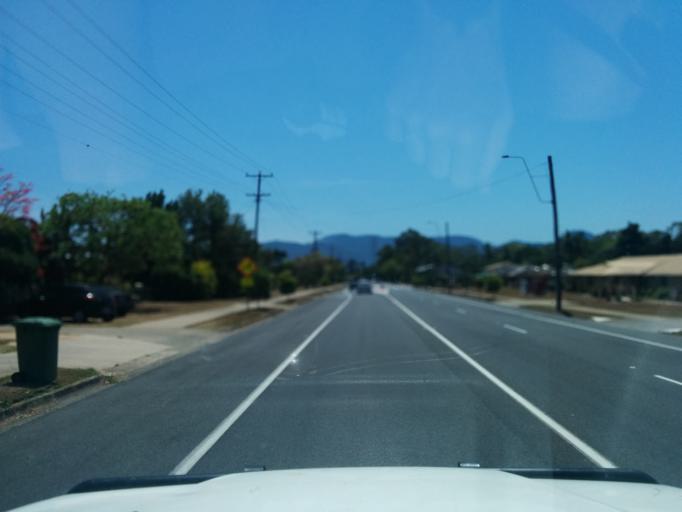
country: AU
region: Queensland
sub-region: Cairns
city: Woree
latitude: -16.9569
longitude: 145.7384
